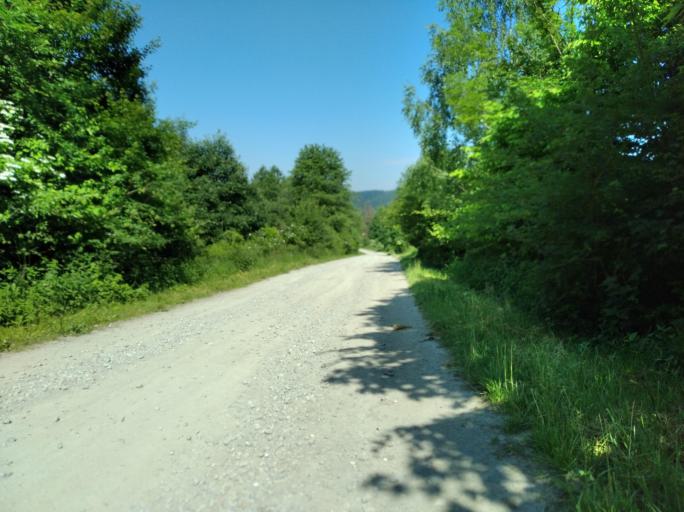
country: PL
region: Subcarpathian Voivodeship
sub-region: Powiat krosnienski
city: Odrzykon
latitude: 49.7681
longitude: 21.7788
